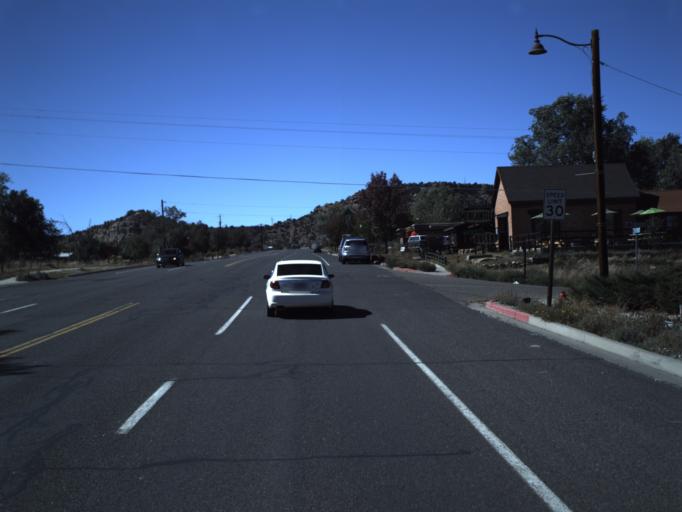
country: US
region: Utah
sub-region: Wayne County
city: Loa
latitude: 37.7704
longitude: -111.6037
